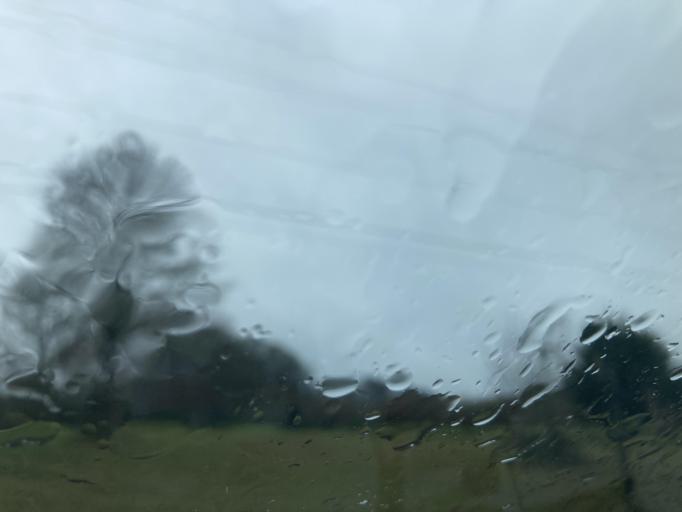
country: US
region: Mississippi
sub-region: Forrest County
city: Rawls Springs
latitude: 31.4887
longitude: -89.3816
